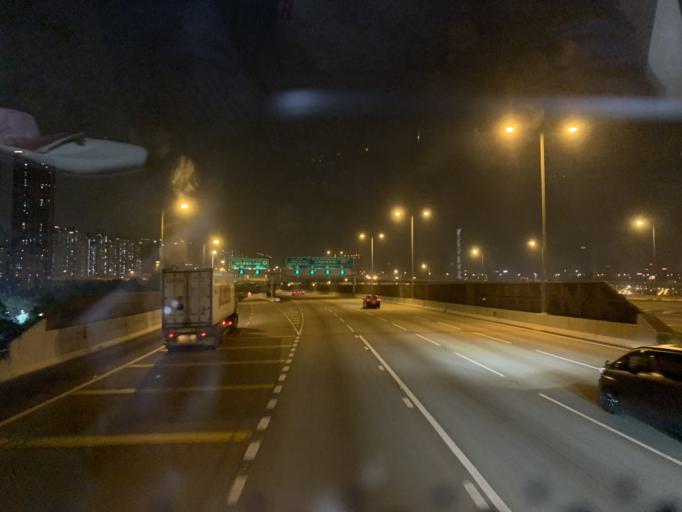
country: HK
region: Sham Shui Po
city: Sham Shui Po
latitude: 22.3353
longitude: 114.1347
